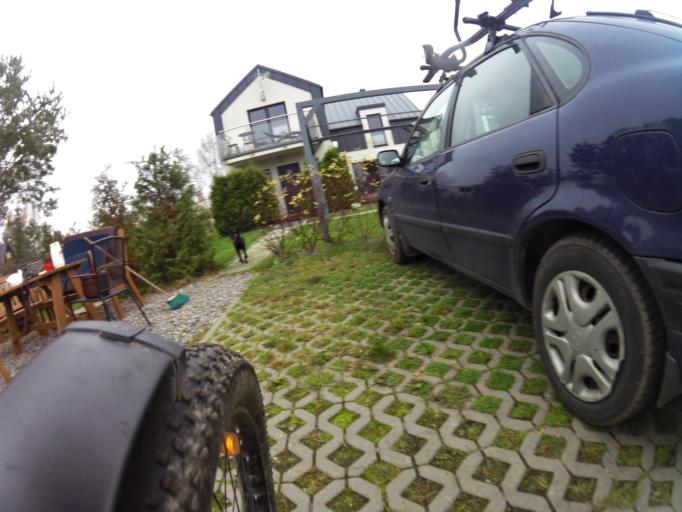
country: PL
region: Pomeranian Voivodeship
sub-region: Powiat pucki
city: Wierzchucino
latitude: 54.8236
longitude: 18.0828
